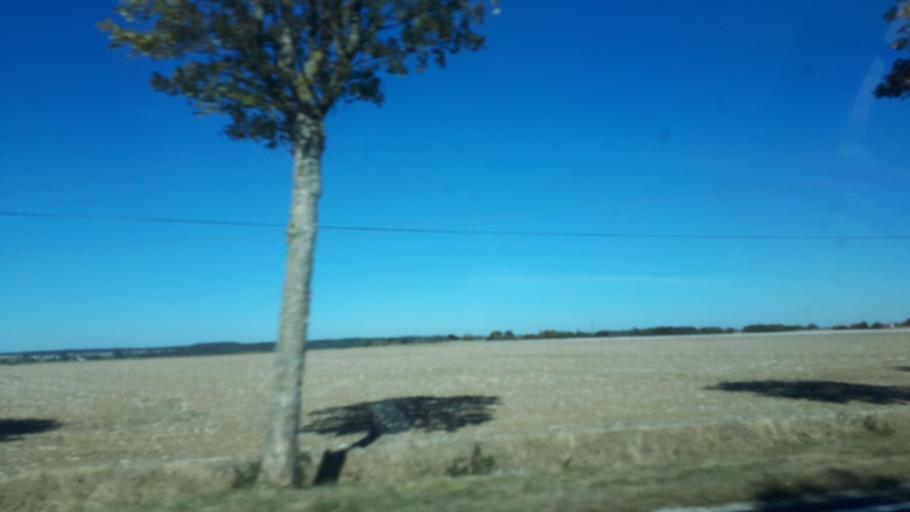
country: FR
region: Centre
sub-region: Departement d'Eure-et-Loir
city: Chateaudun
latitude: 48.0564
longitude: 1.3261
